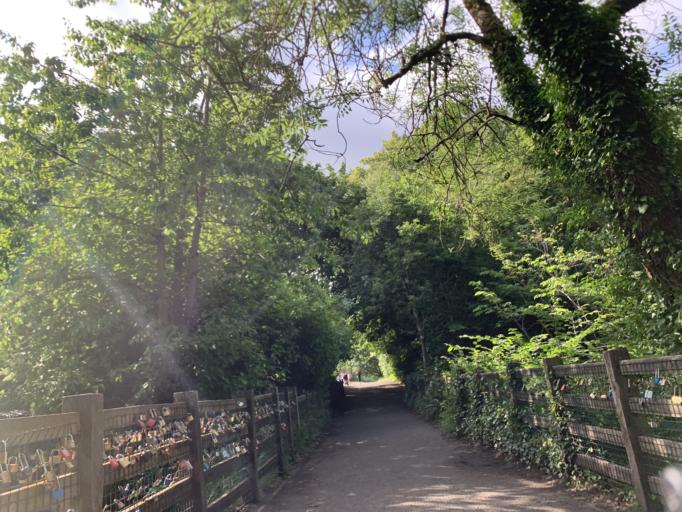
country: GB
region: Scotland
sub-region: East Renfrewshire
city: Giffnock
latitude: 55.7921
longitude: -4.3161
